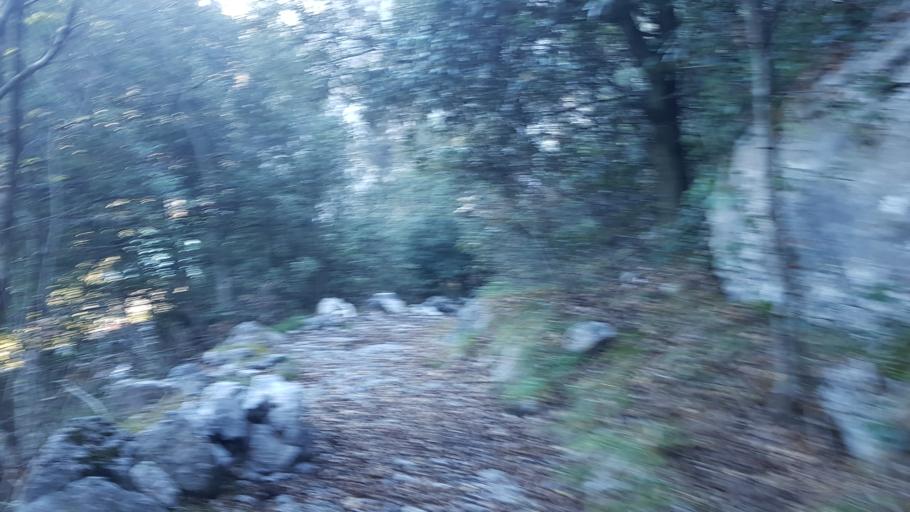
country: IT
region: Trentino-Alto Adige
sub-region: Provincia di Trento
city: Padergnone
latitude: 46.0737
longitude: 10.9792
